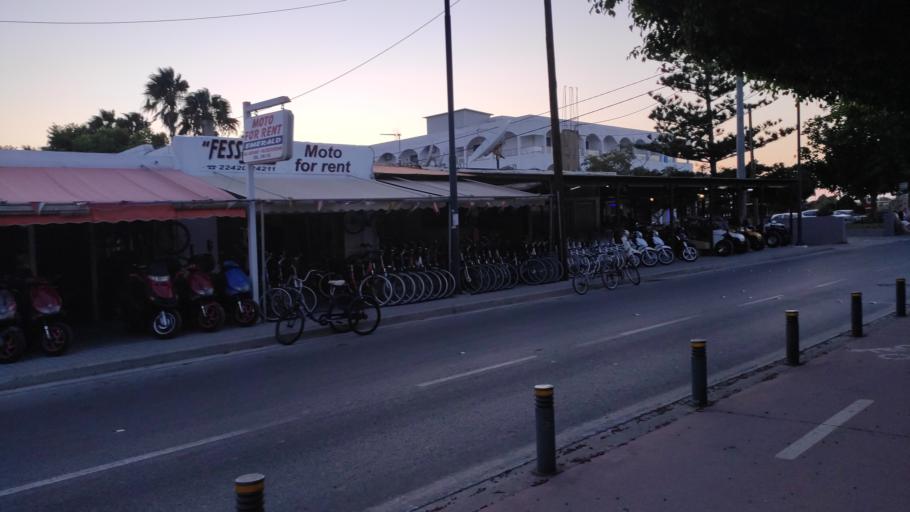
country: GR
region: South Aegean
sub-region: Nomos Dodekanisou
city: Kos
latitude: 36.9120
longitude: 27.2787
